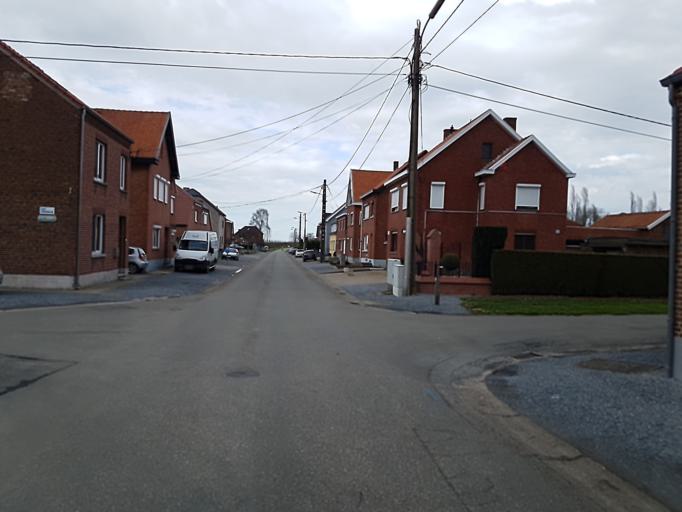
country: BE
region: Flanders
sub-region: Provincie Limburg
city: Heers
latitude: 50.8106
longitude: 5.2611
